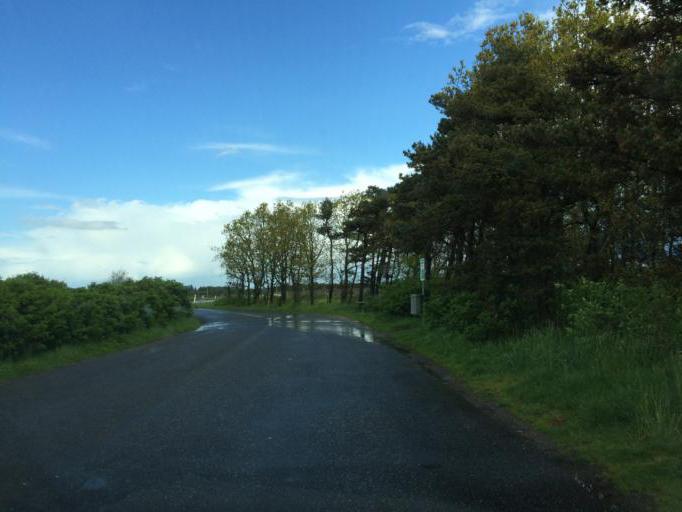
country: DK
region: North Denmark
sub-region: Vesthimmerland Kommune
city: Farso
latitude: 56.6300
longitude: 9.3552
